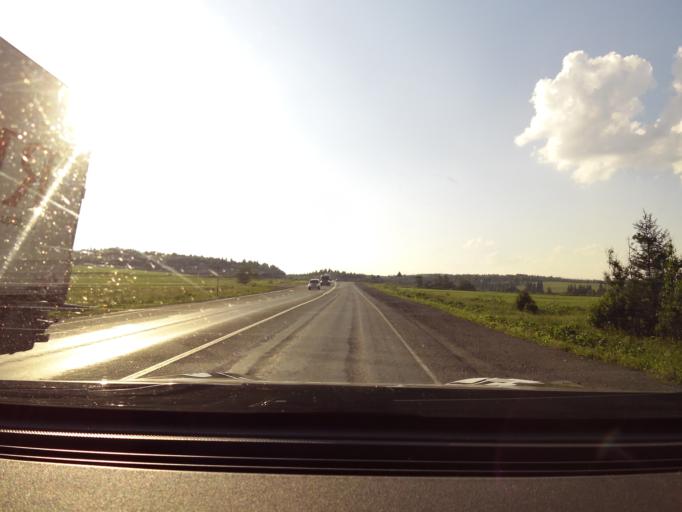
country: RU
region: Sverdlovsk
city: Revda
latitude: 56.8466
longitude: 59.8176
